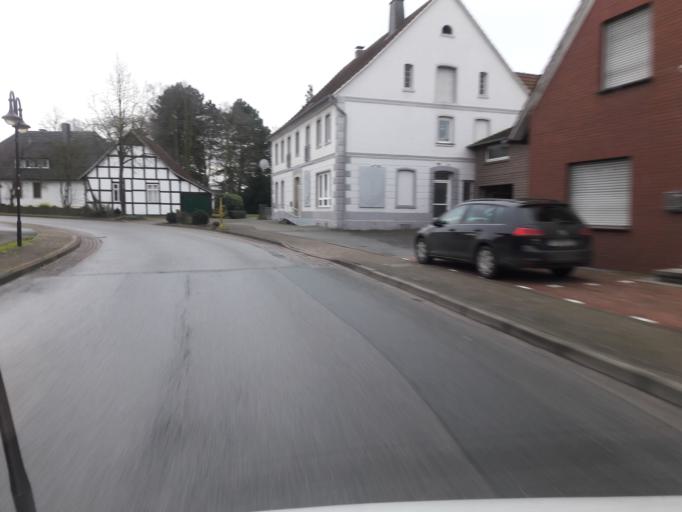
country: DE
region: North Rhine-Westphalia
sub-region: Regierungsbezirk Detmold
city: Hille
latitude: 52.3336
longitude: 8.7473
